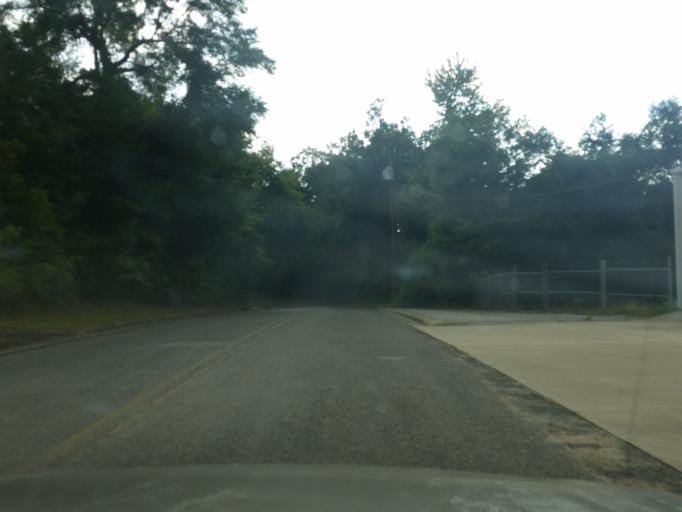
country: US
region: Florida
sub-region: Escambia County
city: Ferry Pass
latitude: 30.5439
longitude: -87.1980
